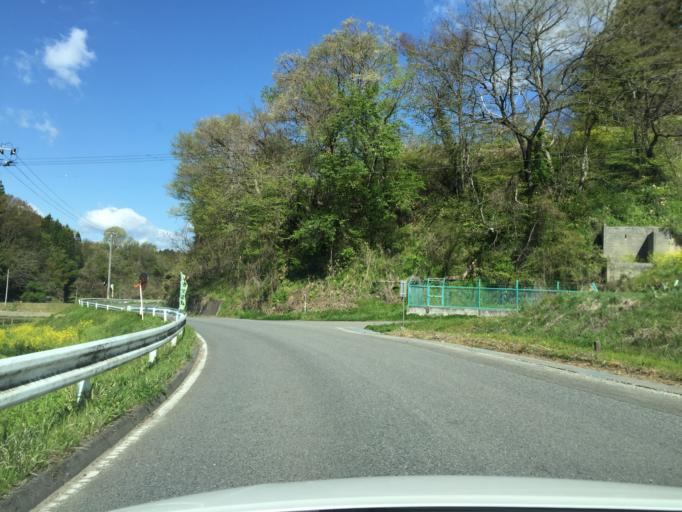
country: JP
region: Fukushima
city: Funehikimachi-funehiki
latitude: 37.5297
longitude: 140.5936
